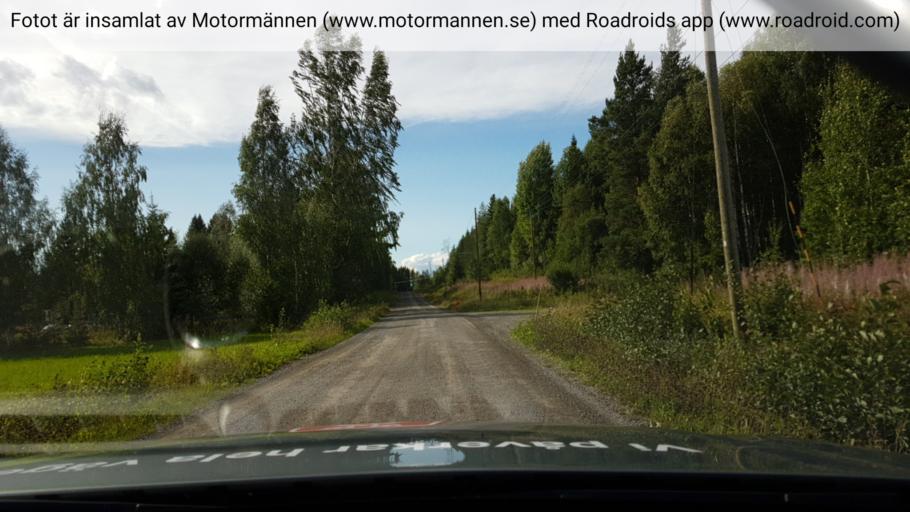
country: SE
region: Jaemtland
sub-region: Braecke Kommun
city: Braecke
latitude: 63.2010
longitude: 15.4273
